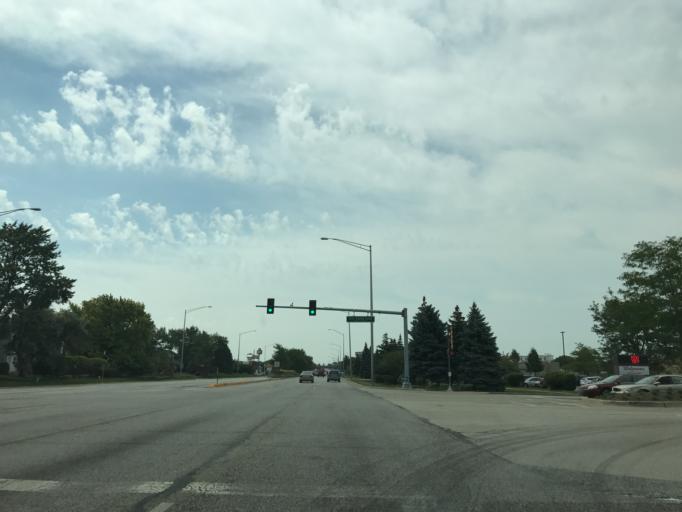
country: US
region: Illinois
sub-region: Will County
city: Bolingbrook
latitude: 41.6917
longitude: -88.0683
